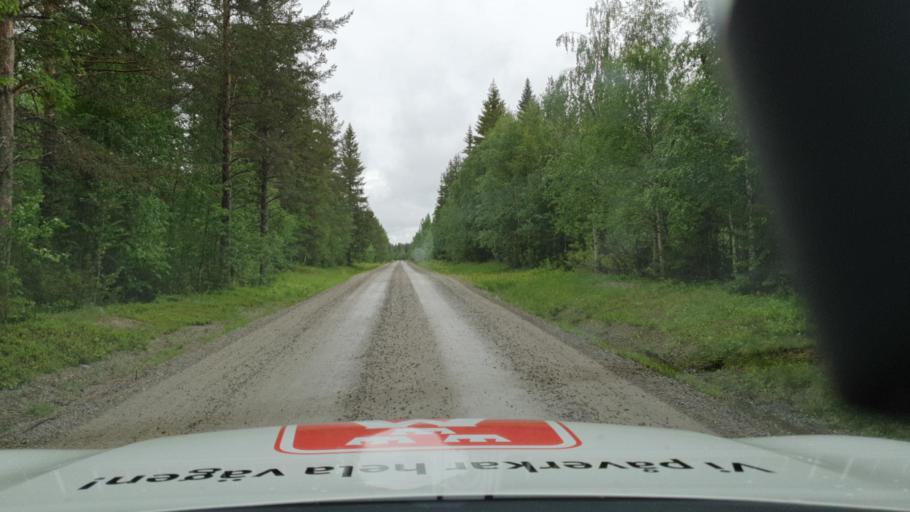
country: SE
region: Vaesterbotten
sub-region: Dorotea Kommun
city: Dorotea
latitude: 64.0049
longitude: 16.7988
